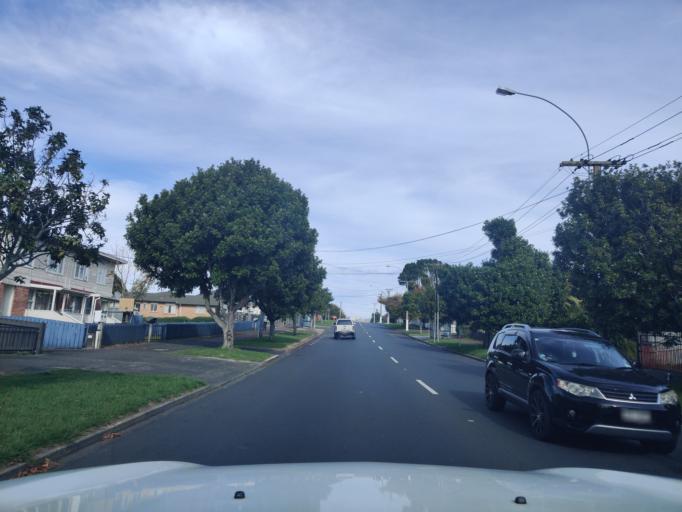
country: NZ
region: Auckland
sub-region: Auckland
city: Tamaki
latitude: -36.8988
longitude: 174.8594
